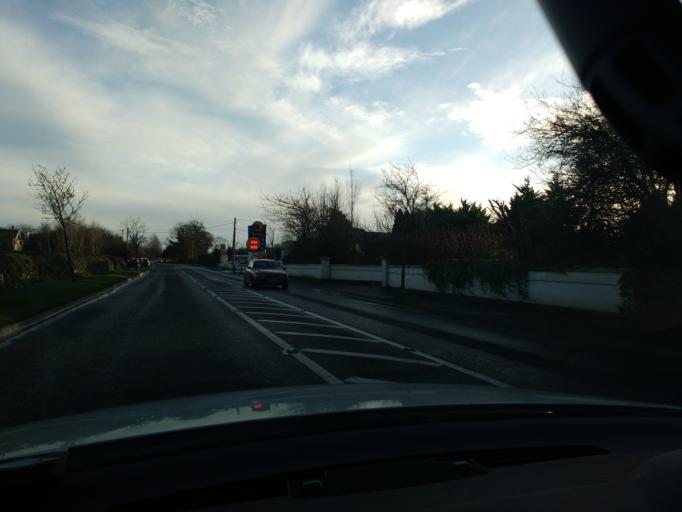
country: IE
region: Munster
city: Thurles
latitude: 52.6669
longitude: -7.8070
